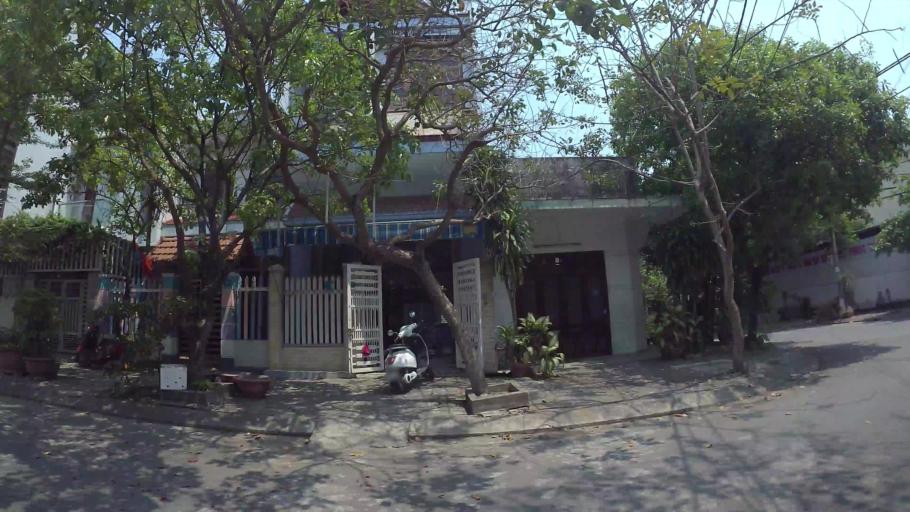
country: VN
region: Da Nang
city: Cam Le
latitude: 16.0168
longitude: 108.2074
